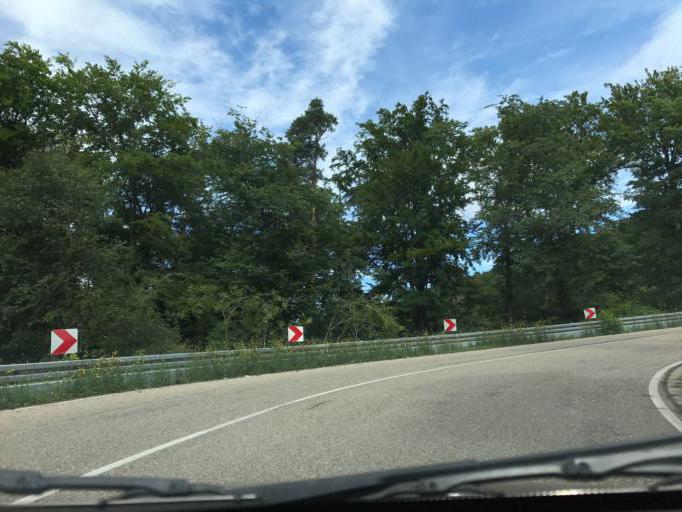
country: DE
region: Baden-Wuerttemberg
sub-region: Regierungsbezirk Stuttgart
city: Esslingen
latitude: 48.7693
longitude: 9.3119
